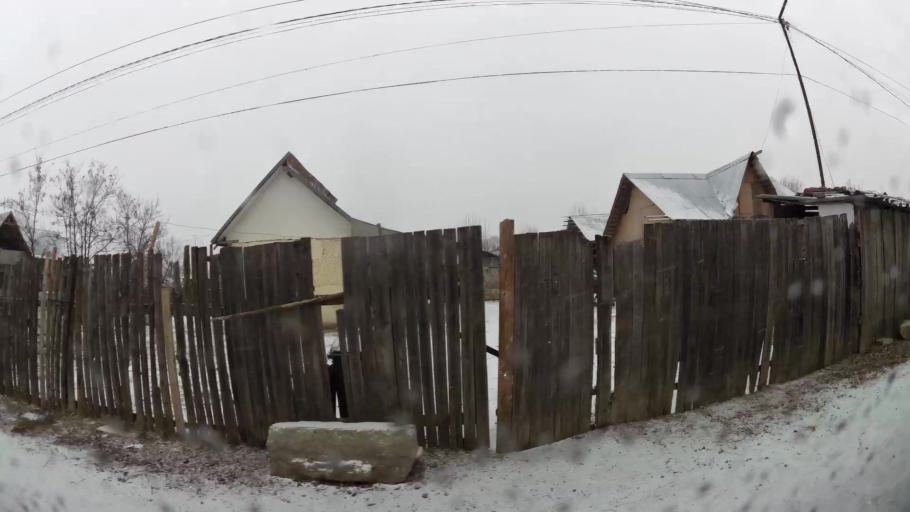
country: RO
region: Dambovita
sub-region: Municipiul Targoviste
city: Targoviste
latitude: 44.9291
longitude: 25.4303
